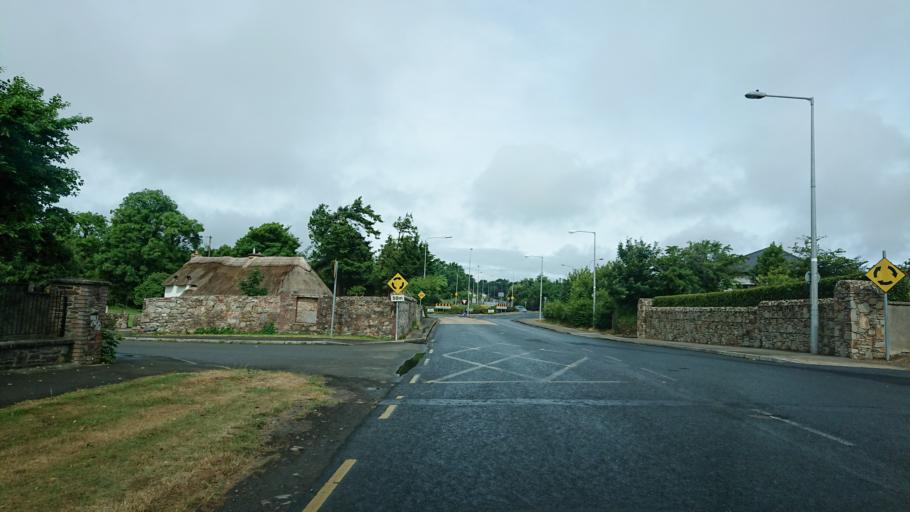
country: IE
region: Munster
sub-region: Waterford
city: Waterford
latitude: 52.2405
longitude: -7.0883
